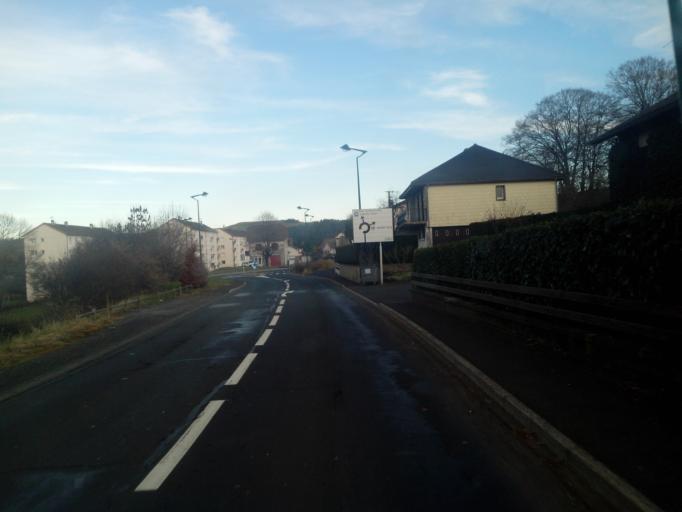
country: FR
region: Auvergne
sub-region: Departement du Cantal
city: Riom-es-Montagnes
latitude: 45.2852
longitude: 2.6456
